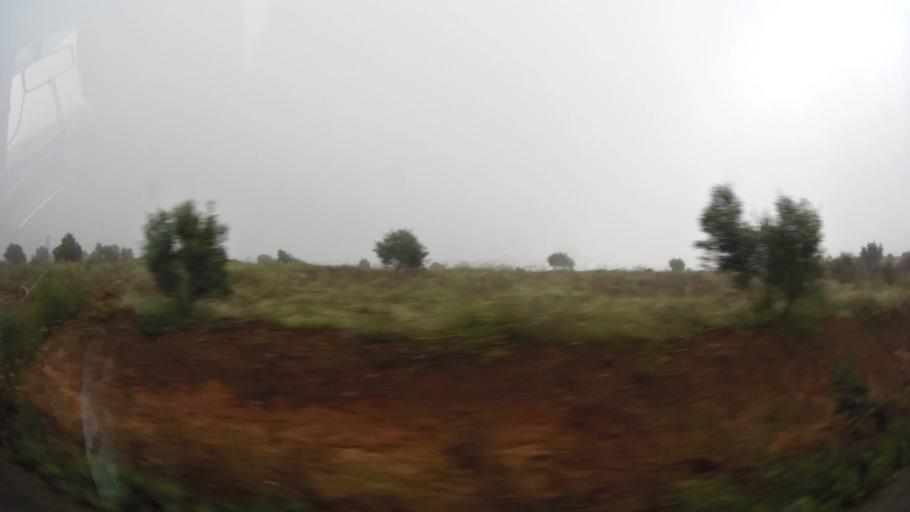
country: MA
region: Oriental
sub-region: Nador
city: Boudinar
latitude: 35.1331
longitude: -3.5965
